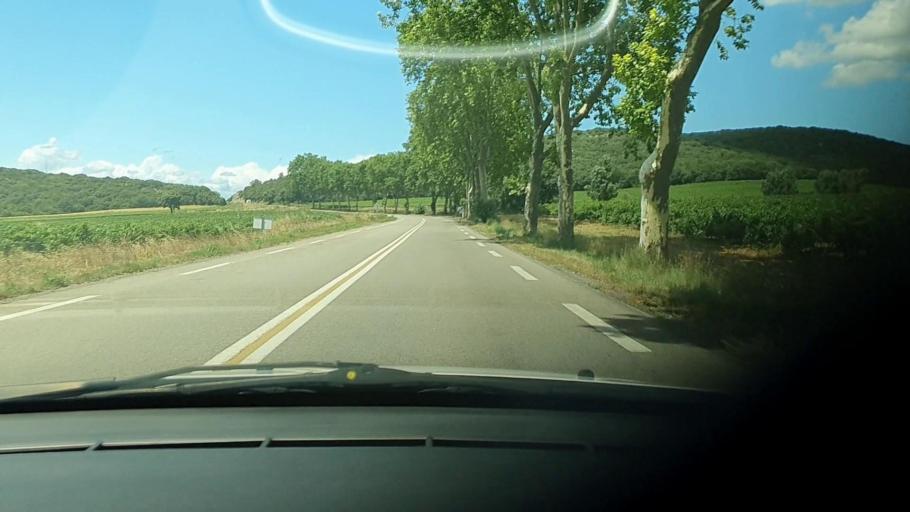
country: FR
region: Languedoc-Roussillon
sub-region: Departement du Gard
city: Moussac
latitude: 44.0599
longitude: 4.2629
